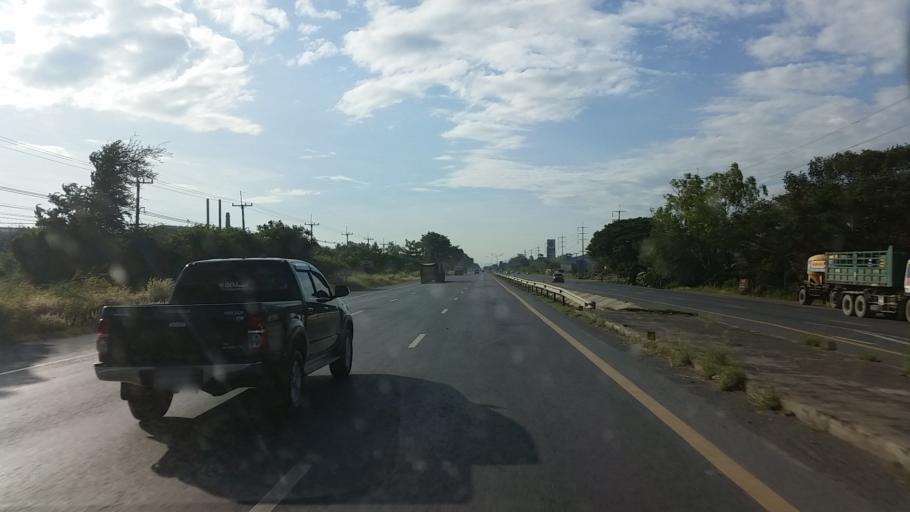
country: TH
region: Sara Buri
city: Chaloem Phra Kiat
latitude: 14.6404
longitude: 100.8869
